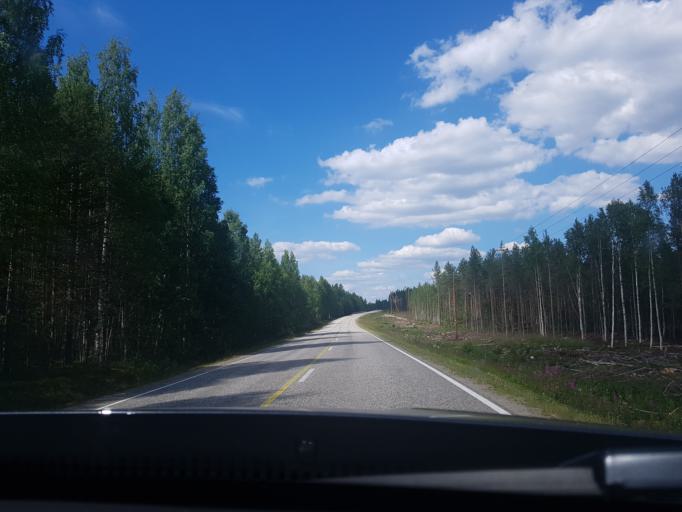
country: FI
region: Kainuu
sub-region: Kehys-Kainuu
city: Kuhmo
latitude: 64.2362
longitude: 29.8175
